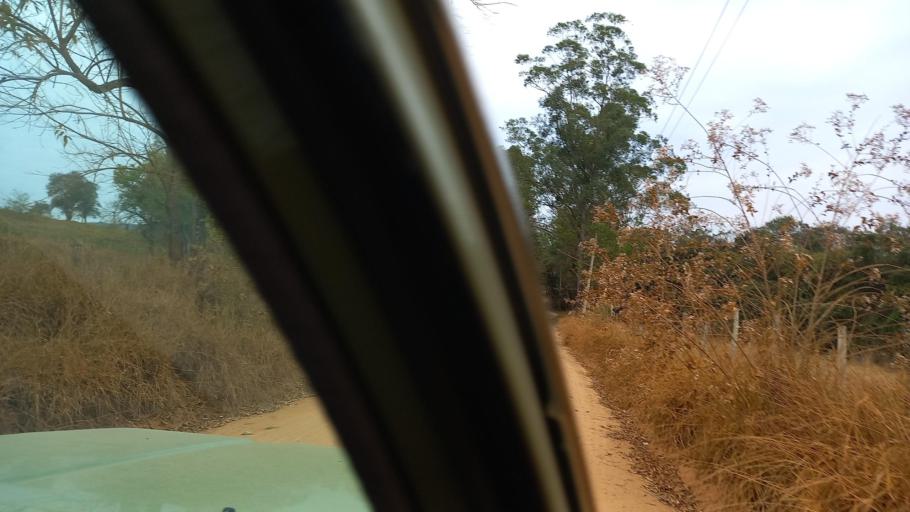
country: BR
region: Sao Paulo
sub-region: Moji-Guacu
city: Mogi-Gaucu
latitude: -22.3062
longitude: -46.8337
